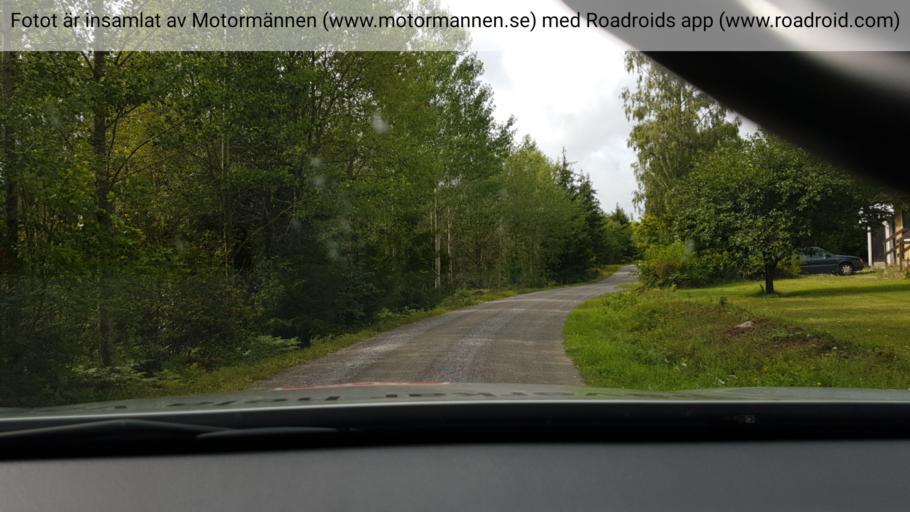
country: SE
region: Uppsala
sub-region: Heby Kommun
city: OEstervala
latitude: 60.0756
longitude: 17.2186
